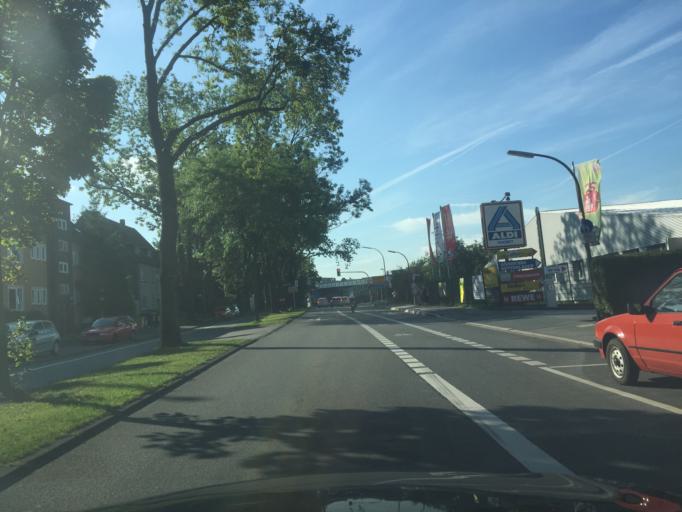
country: DE
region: North Rhine-Westphalia
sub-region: Regierungsbezirk Arnsberg
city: Dortmund
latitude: 51.4979
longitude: 7.4000
